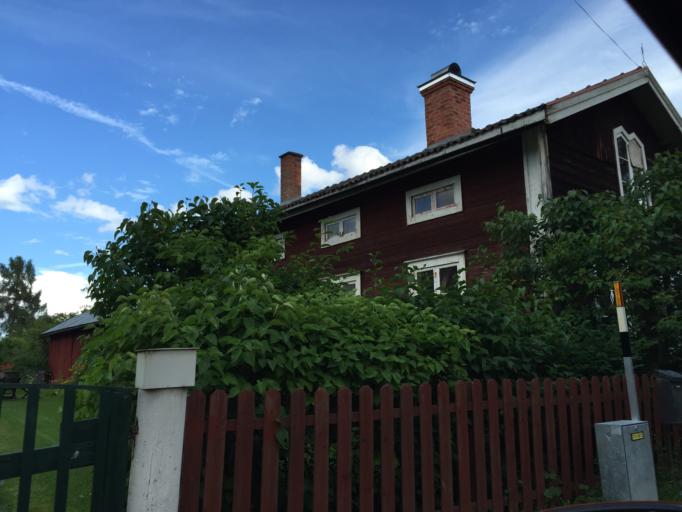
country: SE
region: Gaevleborg
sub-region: Ljusdals Kommun
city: Jaervsoe
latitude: 61.7527
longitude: 16.1704
